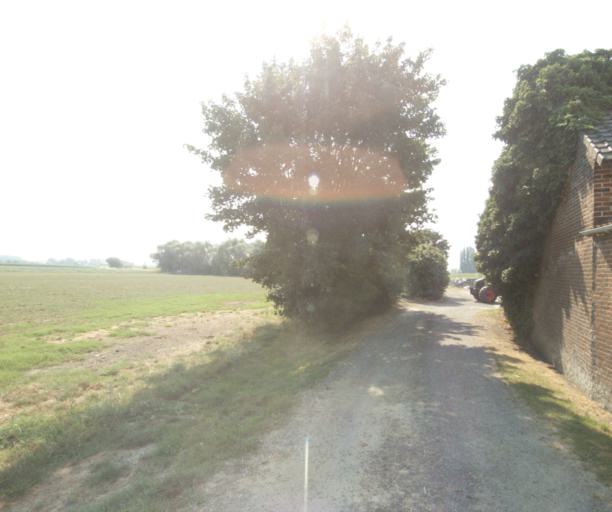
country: FR
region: Nord-Pas-de-Calais
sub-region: Departement du Nord
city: Quesnoy-sur-Deule
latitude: 50.7001
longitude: 3.0002
